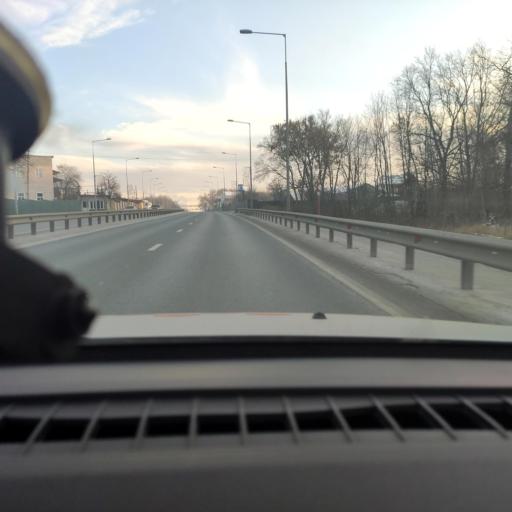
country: RU
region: Samara
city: Petra-Dubrava
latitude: 53.3001
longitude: 50.2426
